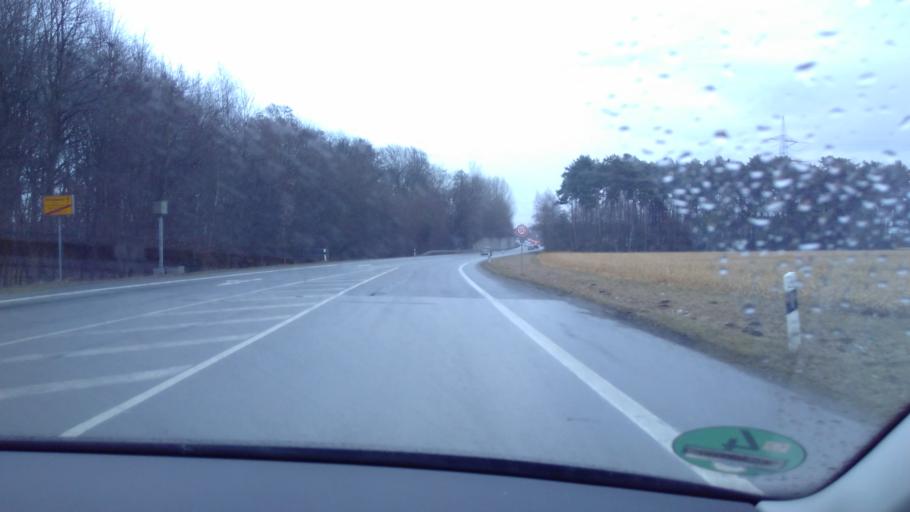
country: DE
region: North Rhine-Westphalia
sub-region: Regierungsbezirk Detmold
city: Oerlinghausen
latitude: 51.9145
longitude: 8.6108
